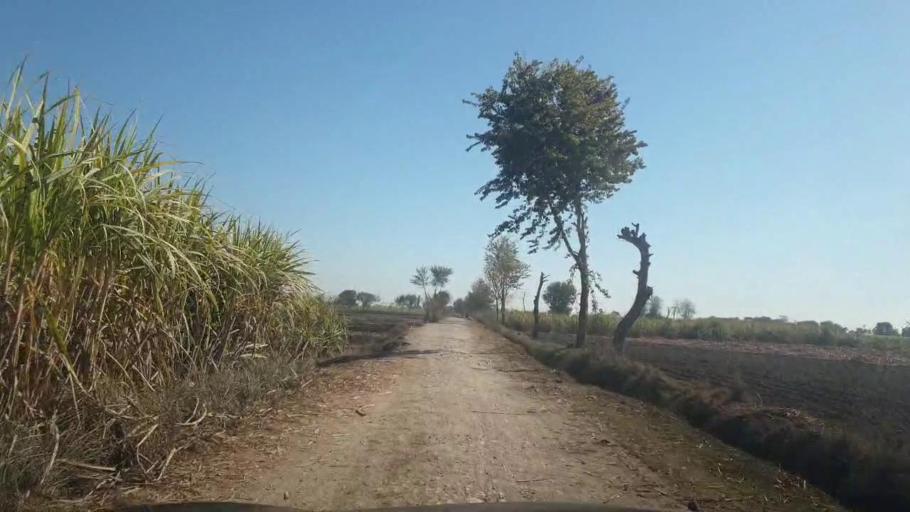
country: PK
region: Sindh
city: Ghotki
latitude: 27.9755
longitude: 69.3303
